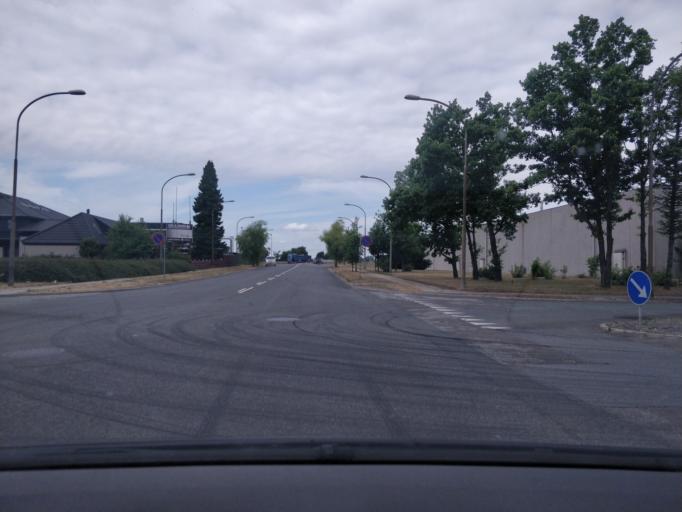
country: DK
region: Capital Region
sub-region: Ishoj Kommune
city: Ishoj
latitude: 55.6176
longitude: 12.3194
